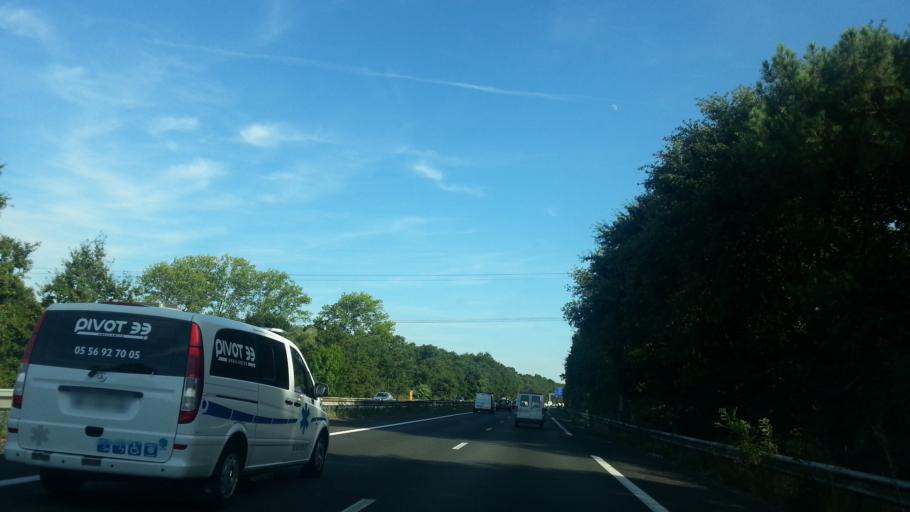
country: FR
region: Aquitaine
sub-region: Departement de la Gironde
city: Ayguemorte-les-Graves
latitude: 44.7030
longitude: -0.5049
